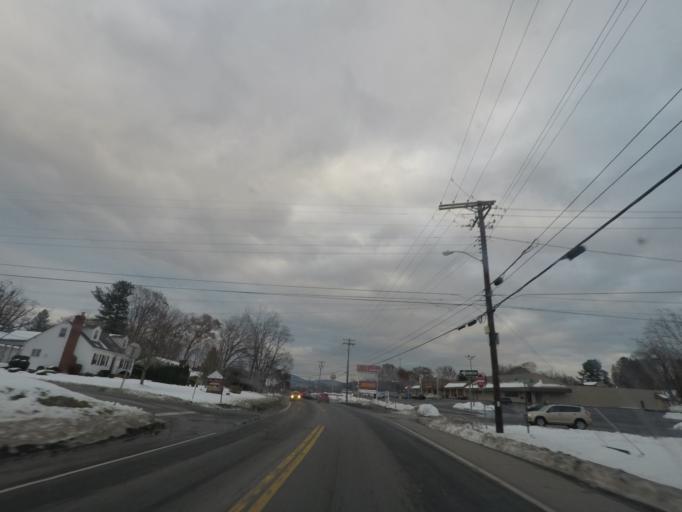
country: US
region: New York
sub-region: Orange County
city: Balmville
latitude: 41.5251
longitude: -74.0328
